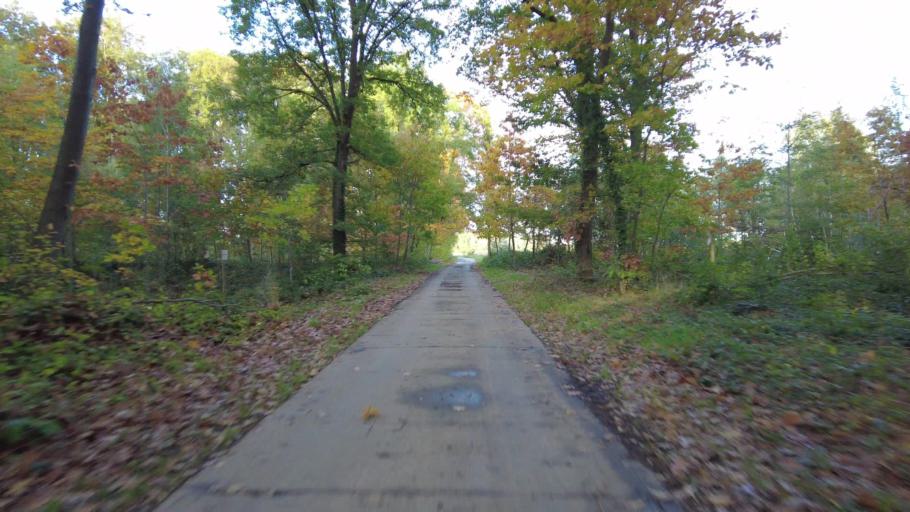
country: BE
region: Flanders
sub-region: Provincie Vlaams-Brabant
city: Hoegaarden
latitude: 50.7355
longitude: 4.9482
